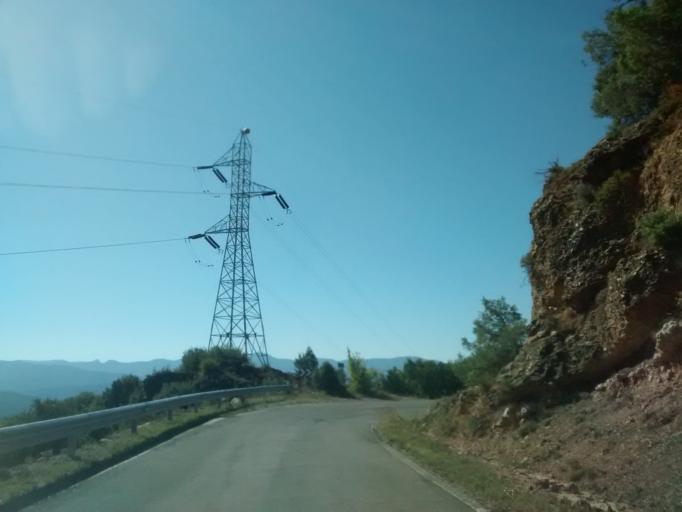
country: ES
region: Aragon
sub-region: Provincia de Huesca
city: Jaca
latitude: 42.4814
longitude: -0.5683
